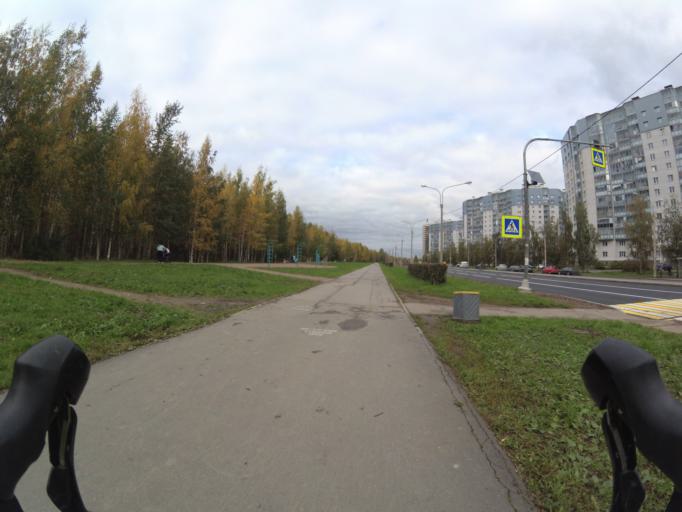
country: RU
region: Leningrad
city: Untolovo
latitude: 59.9960
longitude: 30.1924
